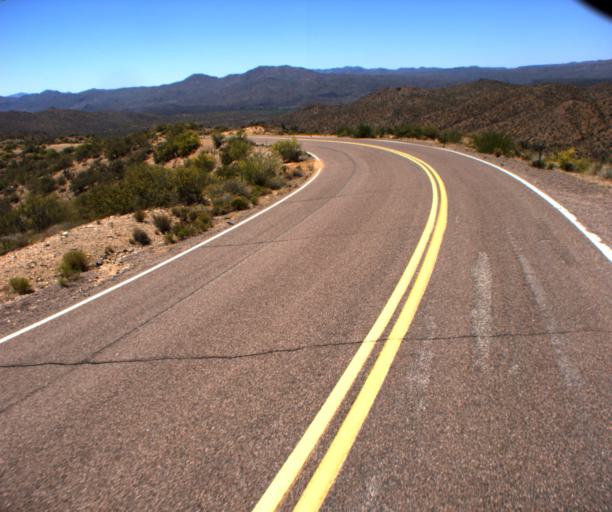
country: US
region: Arizona
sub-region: Yavapai County
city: Bagdad
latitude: 34.4611
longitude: -112.9980
